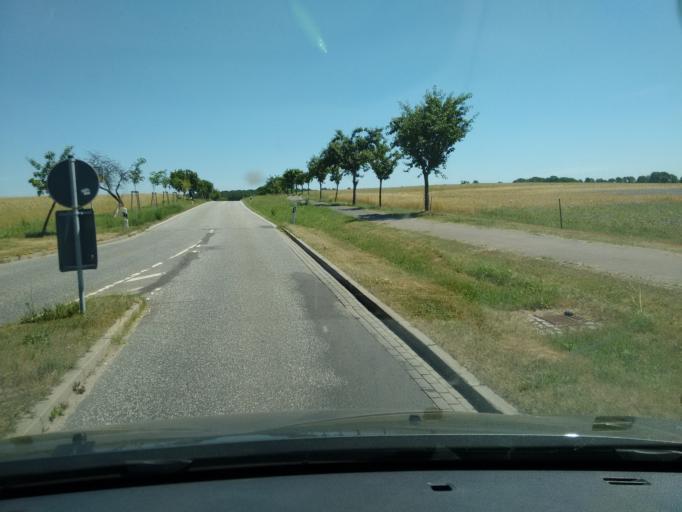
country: DE
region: Brandenburg
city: Beeskow
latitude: 52.1951
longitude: 14.3095
